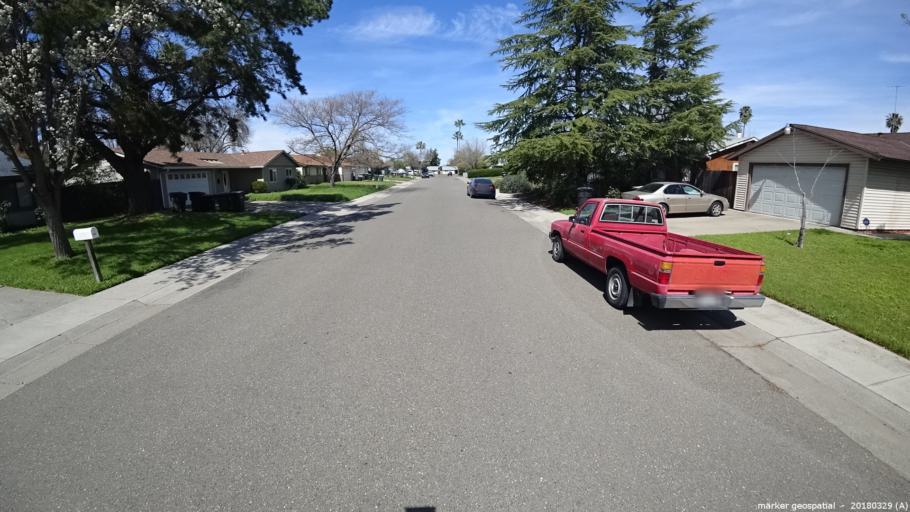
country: US
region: California
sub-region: Sacramento County
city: Rosemont
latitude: 38.5416
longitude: -121.3540
